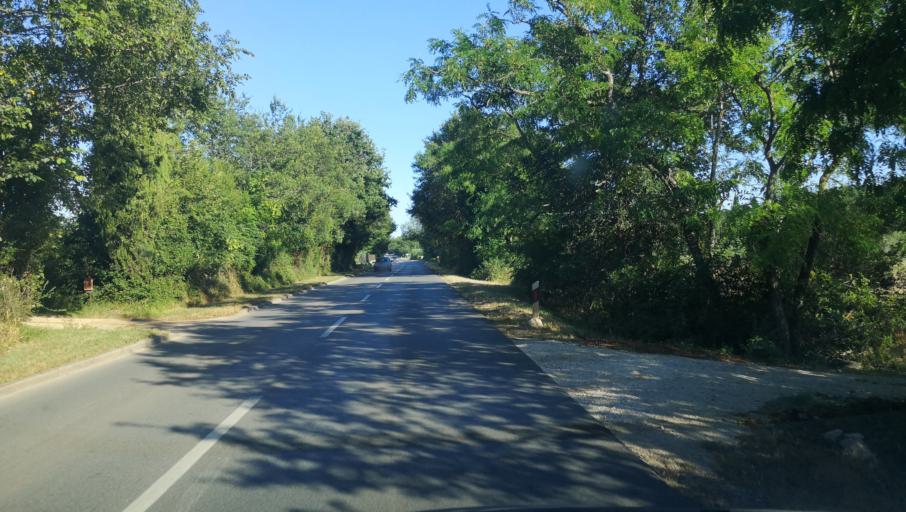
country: HR
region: Istarska
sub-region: Grad Rovinj
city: Rovinj
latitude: 45.0702
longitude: 13.6818
